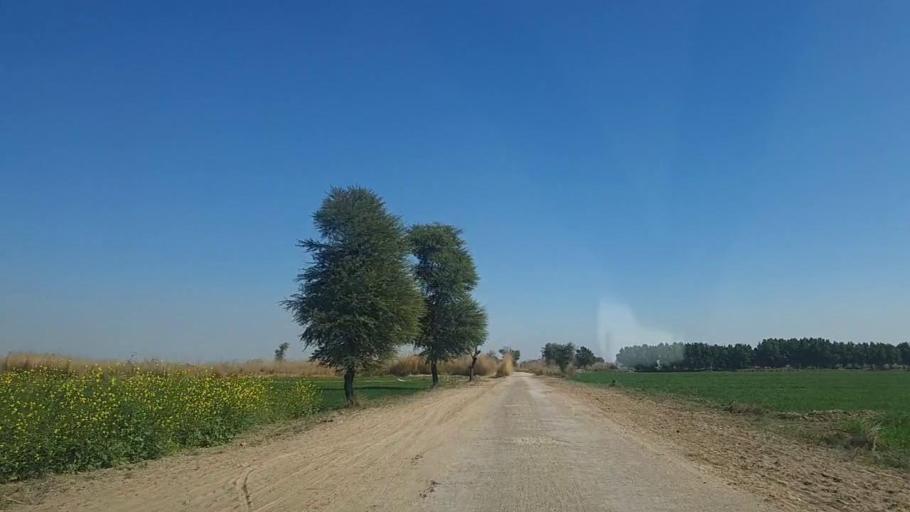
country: PK
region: Sindh
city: Khadro
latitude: 26.2093
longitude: 68.8630
